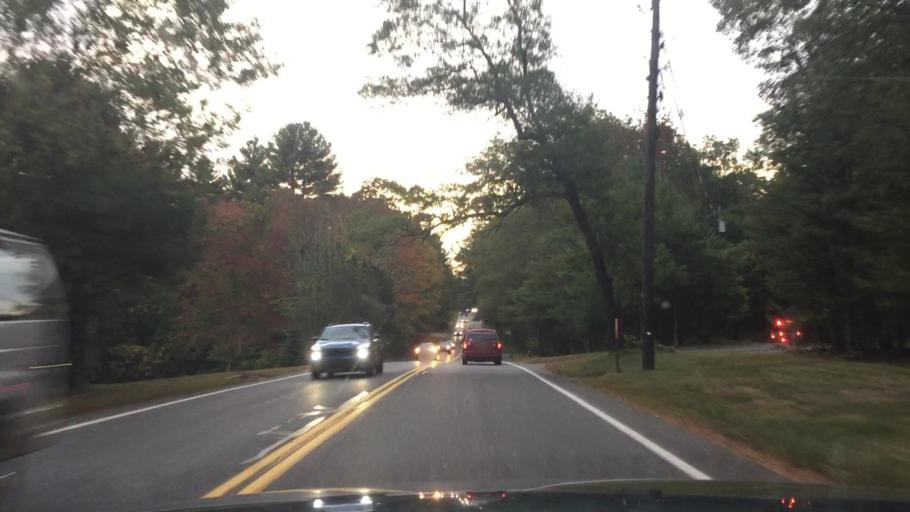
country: US
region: Massachusetts
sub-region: Norfolk County
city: Walpole
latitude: 42.1606
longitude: -71.2775
